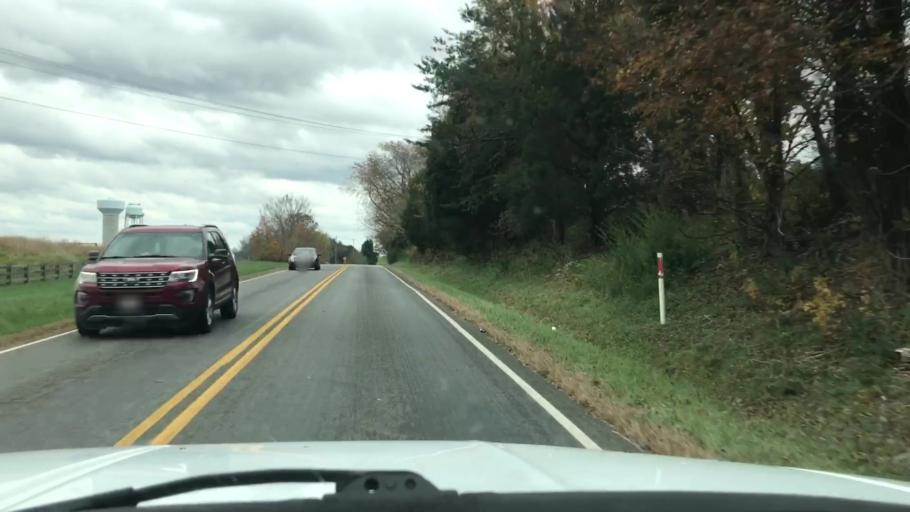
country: US
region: Virginia
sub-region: Goochland County
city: Goochland
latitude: 37.6505
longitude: -77.8429
